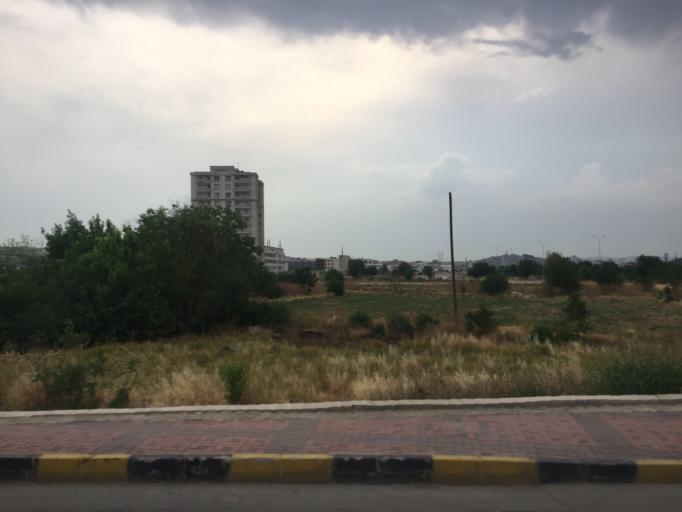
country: TR
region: Gaziantep
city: Gaziantep
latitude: 37.0564
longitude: 37.4157
